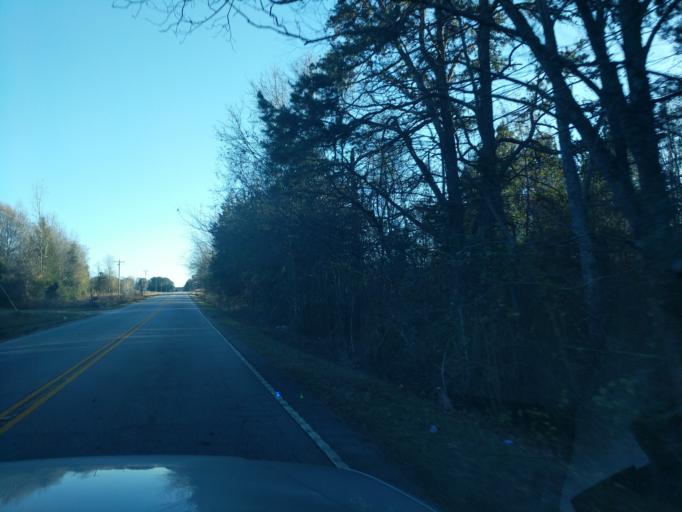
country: US
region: South Carolina
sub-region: Oconee County
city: Westminster
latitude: 34.6386
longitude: -83.0614
